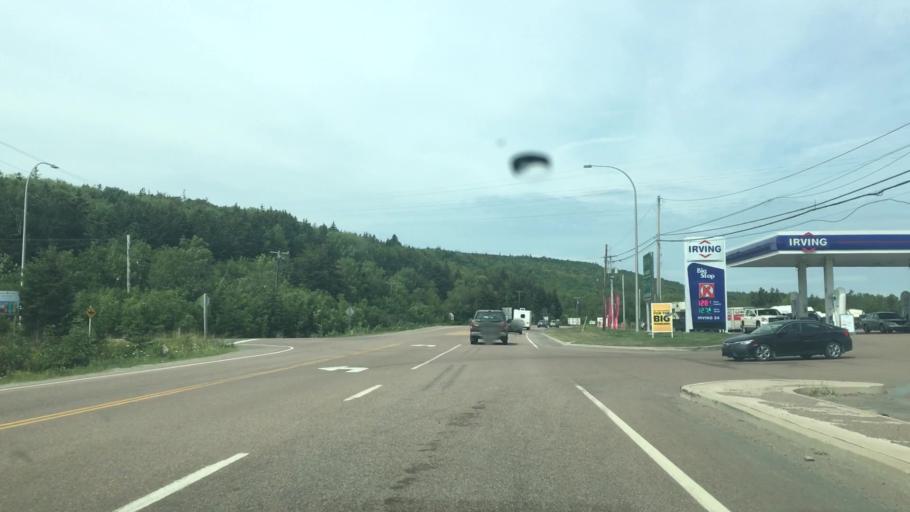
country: CA
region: Nova Scotia
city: Port Hawkesbury
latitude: 45.6486
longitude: -61.4388
